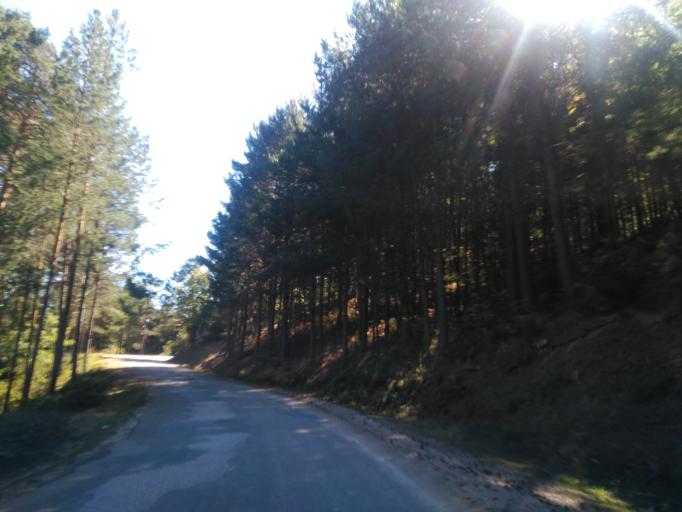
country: ES
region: Castille and Leon
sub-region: Provincia de Soria
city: Vinuesa
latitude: 41.9722
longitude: -2.7938
